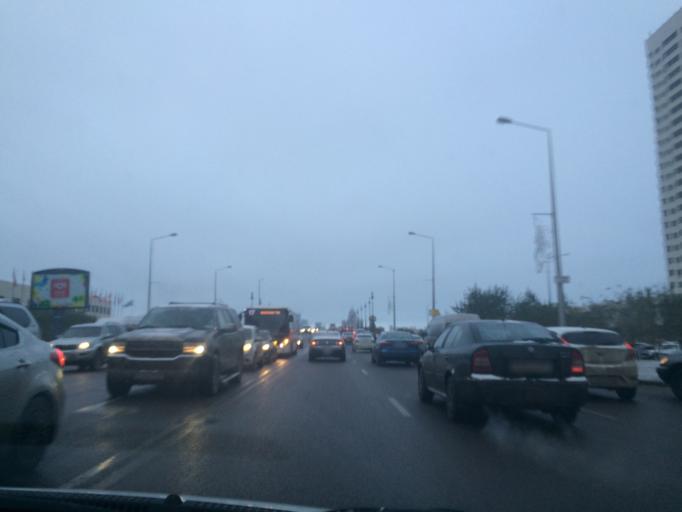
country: KZ
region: Astana Qalasy
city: Astana
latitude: 51.1605
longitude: 71.4104
